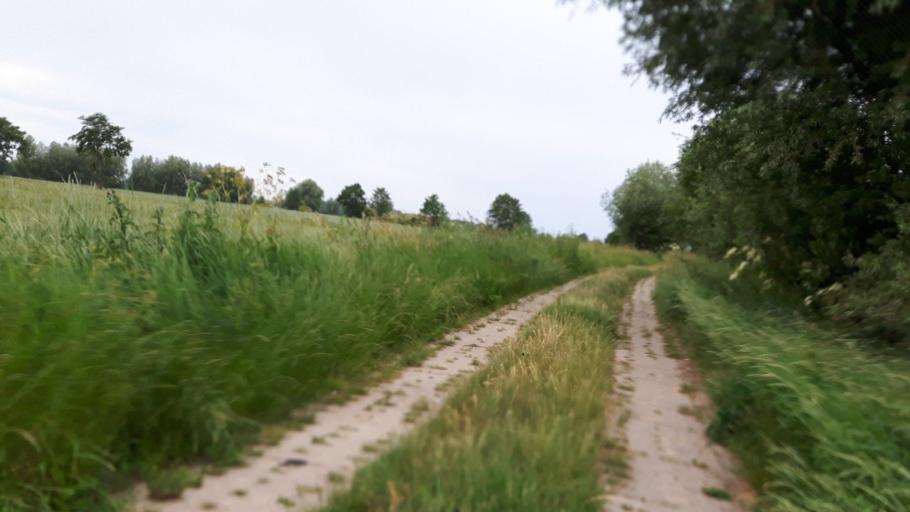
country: PL
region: Warmian-Masurian Voivodeship
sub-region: Powiat elblaski
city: Elblag
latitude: 54.2085
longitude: 19.3396
